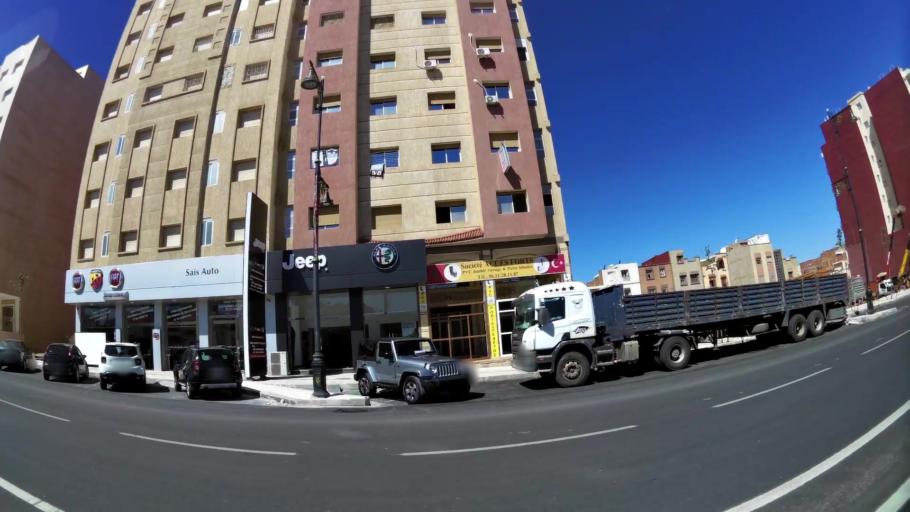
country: MA
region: Meknes-Tafilalet
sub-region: Meknes
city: Meknes
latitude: 33.8573
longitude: -5.5286
